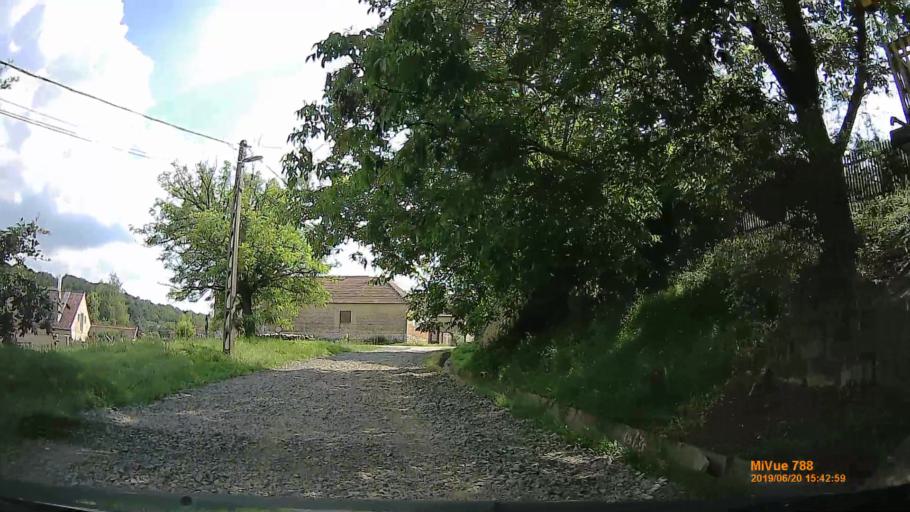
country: HU
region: Baranya
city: Kozarmisleny
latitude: 45.9840
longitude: 18.2631
